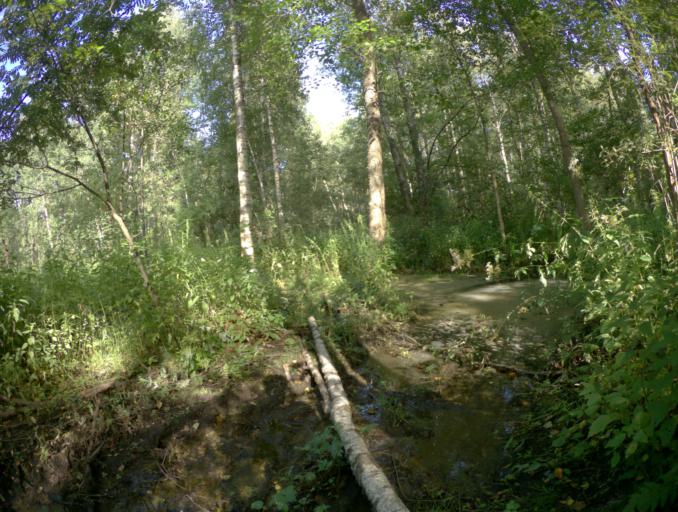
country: RU
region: Vladimir
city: Bogolyubovo
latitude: 56.1332
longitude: 40.5144
